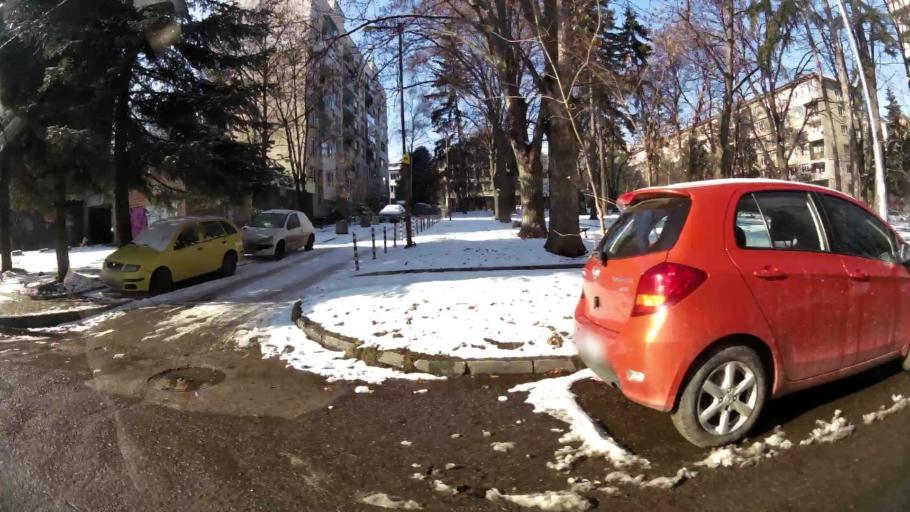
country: BG
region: Sofia-Capital
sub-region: Stolichna Obshtina
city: Sofia
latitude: 42.6782
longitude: 23.3128
